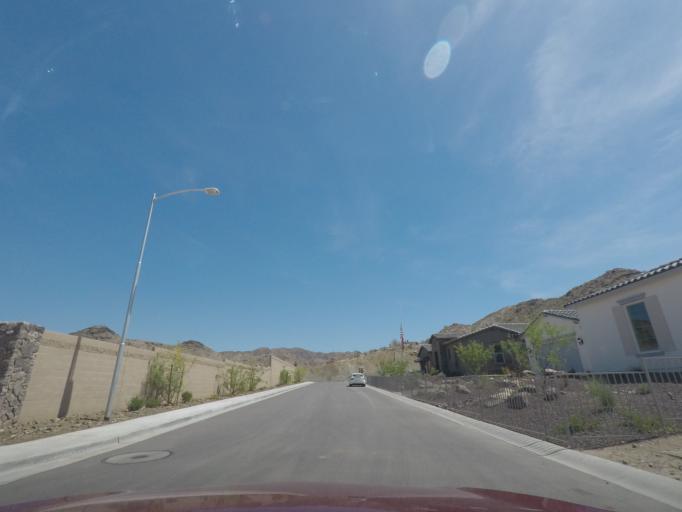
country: US
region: Arizona
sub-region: Maricopa County
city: Laveen
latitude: 33.2981
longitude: -112.1366
